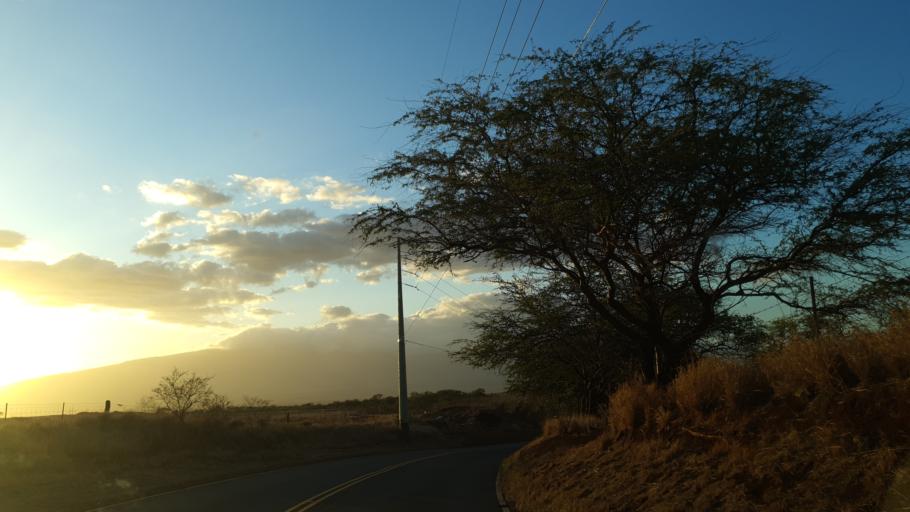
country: US
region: Hawaii
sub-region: Maui County
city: Pukalani
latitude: 20.8025
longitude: -156.3764
